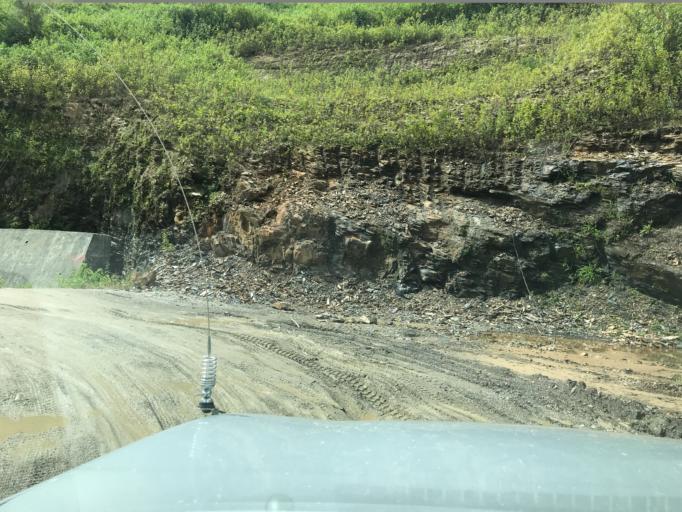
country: TL
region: Aileu
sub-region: Aileu Villa
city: Aileu
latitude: -8.6608
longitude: 125.5505
